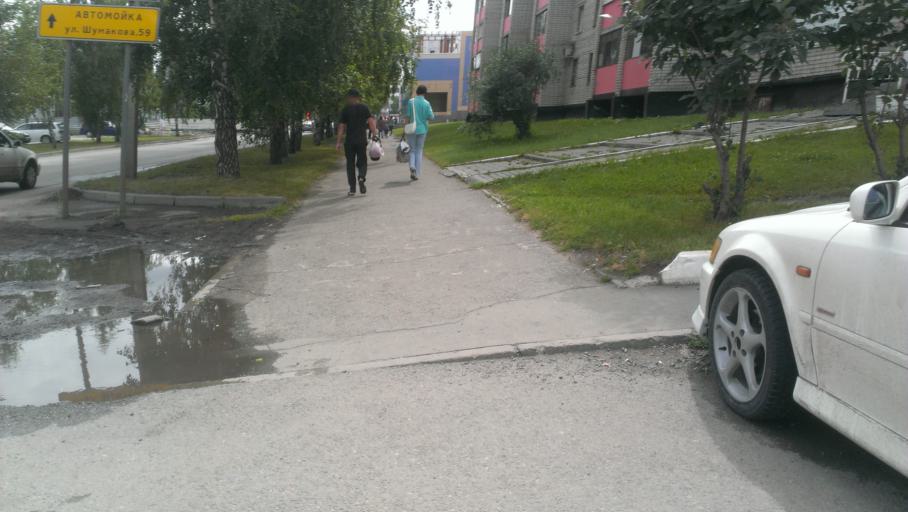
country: RU
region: Altai Krai
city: Novosilikatnyy
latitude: 53.3371
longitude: 83.6773
